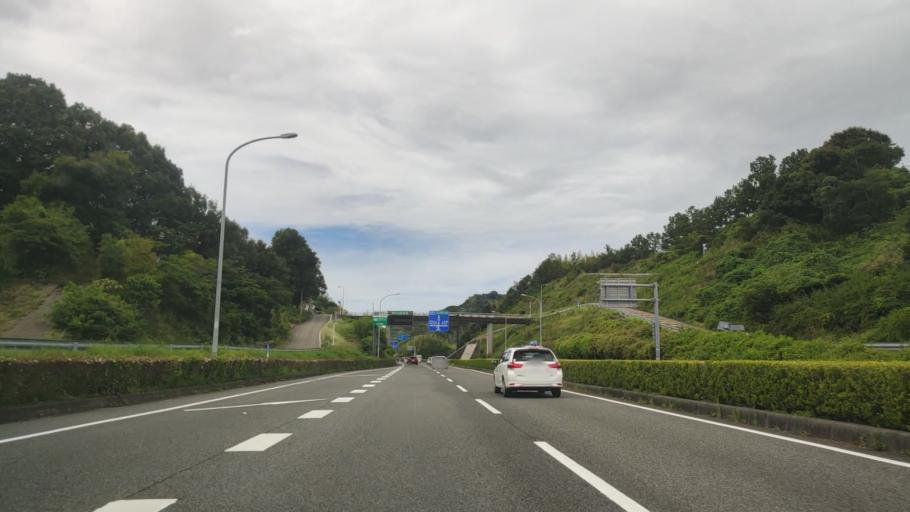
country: JP
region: Wakayama
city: Tanabe
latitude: 33.7445
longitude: 135.3829
